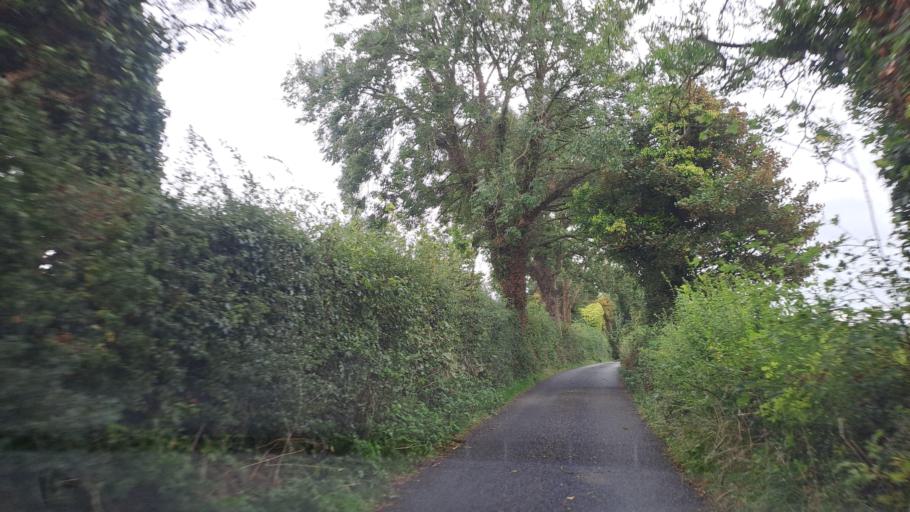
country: IE
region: Ulster
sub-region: An Cabhan
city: Kingscourt
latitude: 53.9548
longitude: -6.7764
